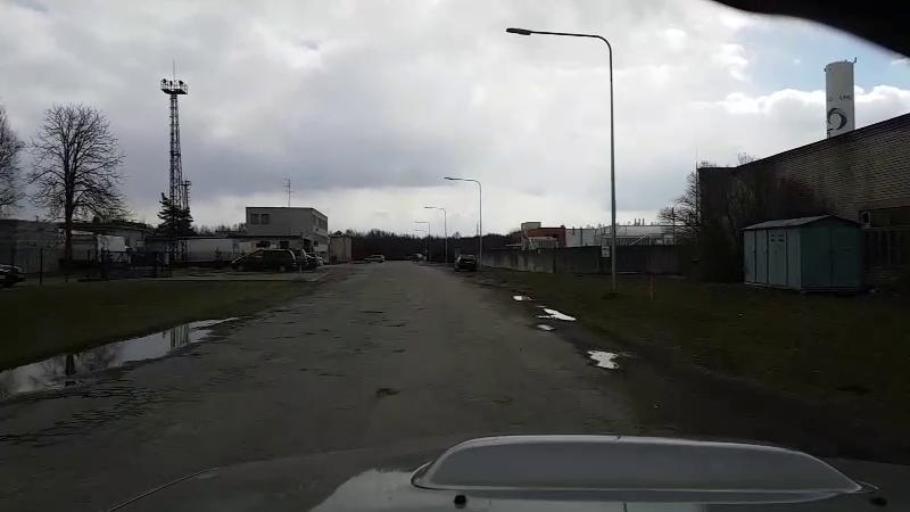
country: EE
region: Jaervamaa
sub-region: Paide linn
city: Paide
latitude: 58.8805
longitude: 25.5611
